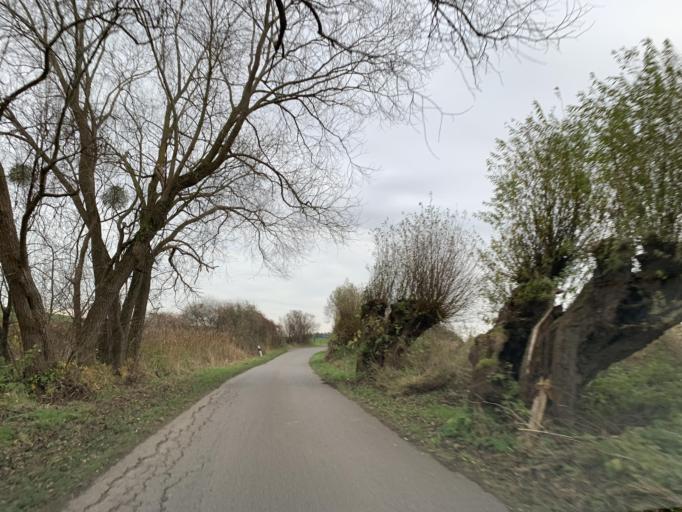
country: DE
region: Mecklenburg-Vorpommern
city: Carpin
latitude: 53.4013
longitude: 13.2044
